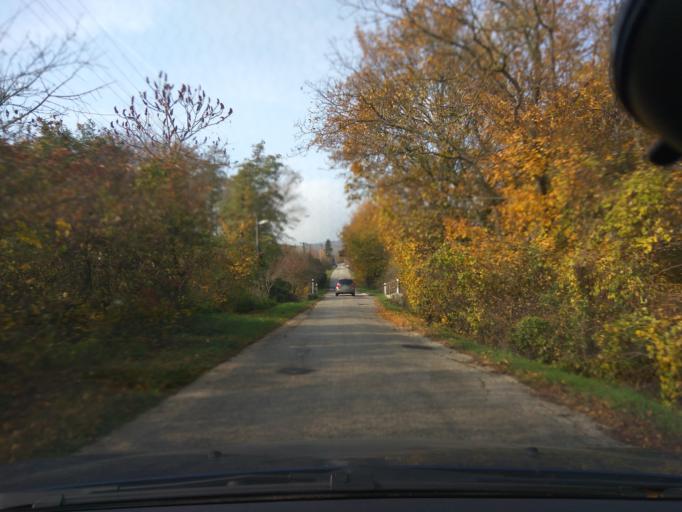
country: SK
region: Trnavsky
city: Vrbove
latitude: 48.6774
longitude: 17.7313
